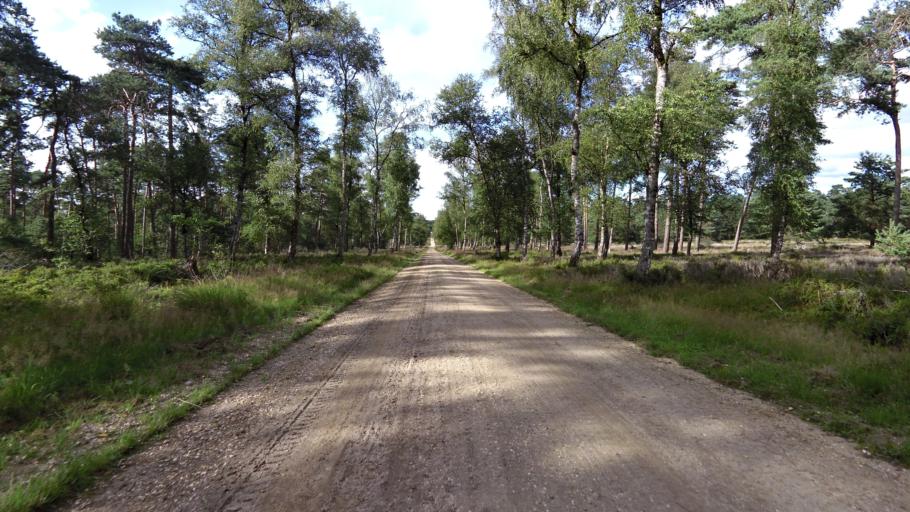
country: NL
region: Gelderland
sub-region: Gemeente Apeldoorn
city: Uddel
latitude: 52.2820
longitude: 5.8667
